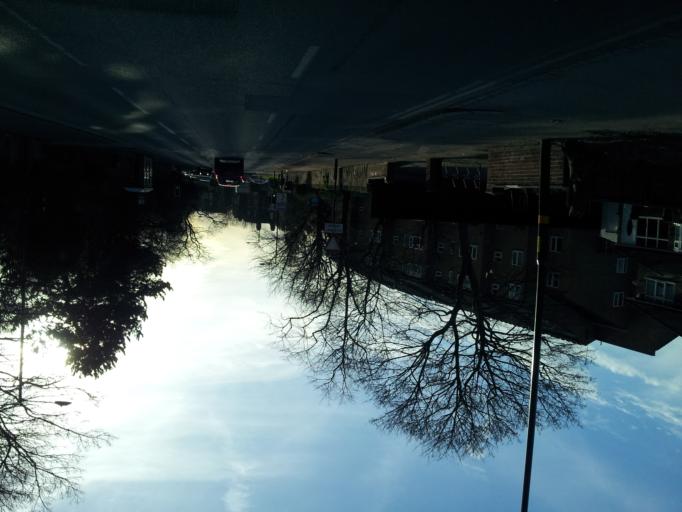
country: GB
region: England
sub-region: City and Borough of Birmingham
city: Birmingham
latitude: 52.5136
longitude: -1.8513
